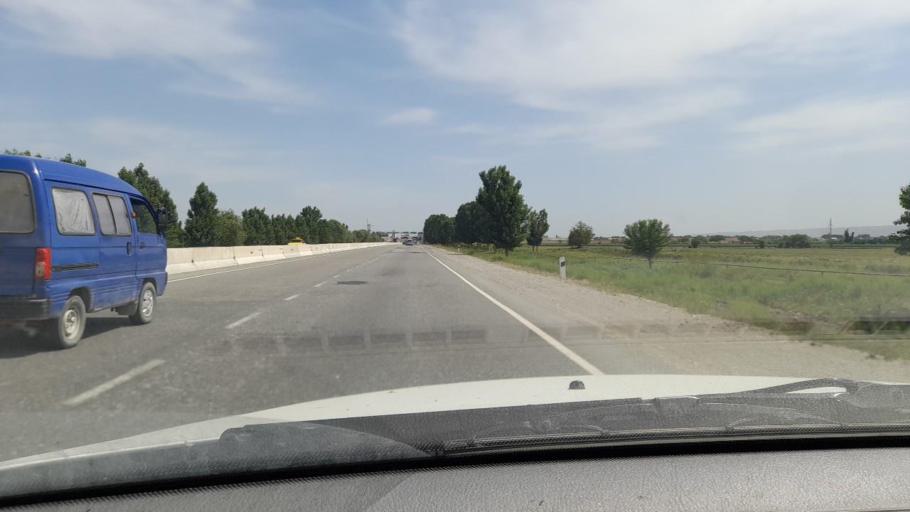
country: UZ
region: Navoiy
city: Karmana Shahri
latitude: 40.1214
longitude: 65.4811
